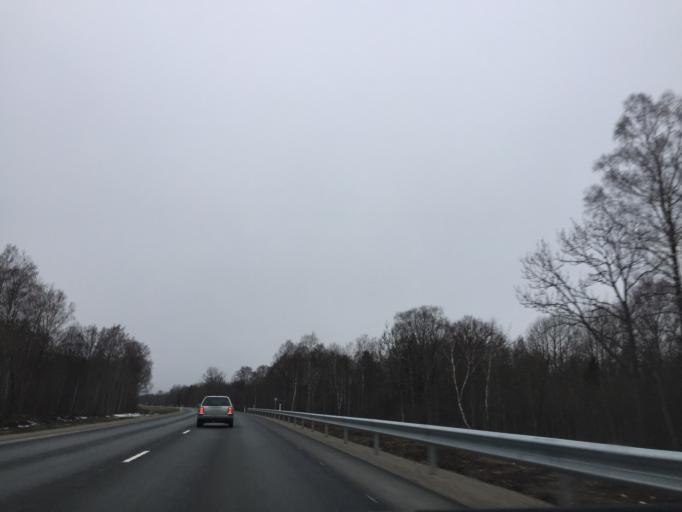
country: EE
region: Laeaene
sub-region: Lihula vald
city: Lihula
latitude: 58.6245
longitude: 23.6458
